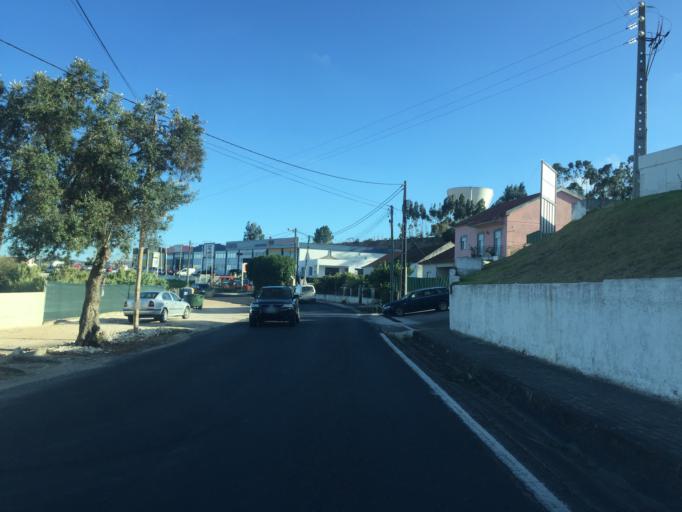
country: PT
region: Lisbon
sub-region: Torres Vedras
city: Torres Vedras
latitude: 39.1132
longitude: -9.2629
